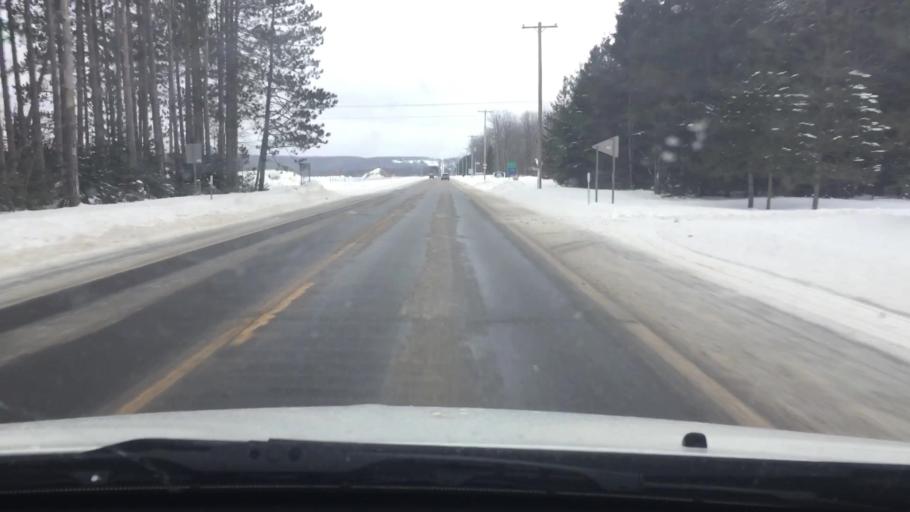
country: US
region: Michigan
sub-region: Charlevoix County
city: East Jordan
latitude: 45.1325
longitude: -85.0979
